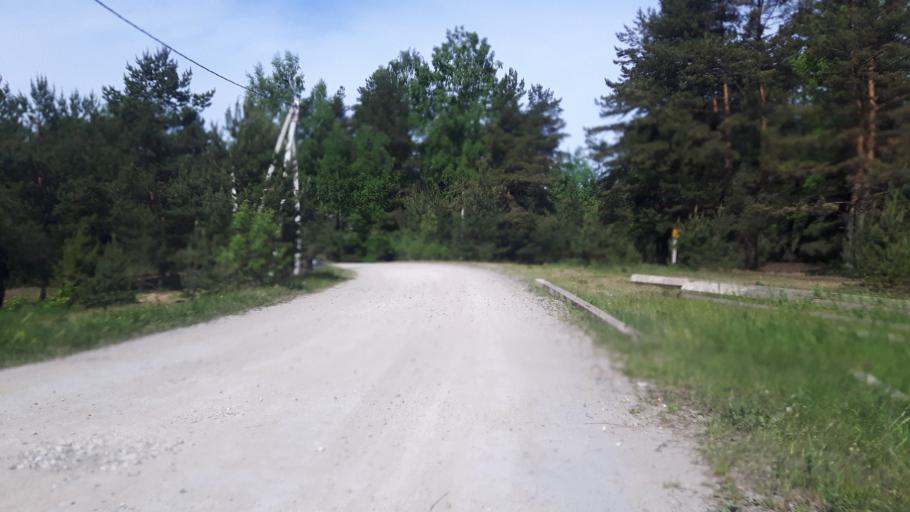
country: RU
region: Leningrad
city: Vistino
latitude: 59.6746
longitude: 28.4439
